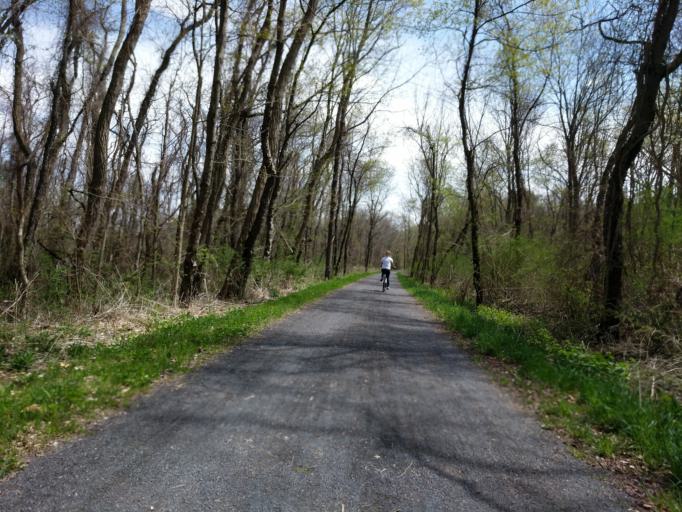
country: US
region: New York
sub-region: Tompkins County
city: Northwest Ithaca
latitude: 42.5059
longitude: -76.5509
